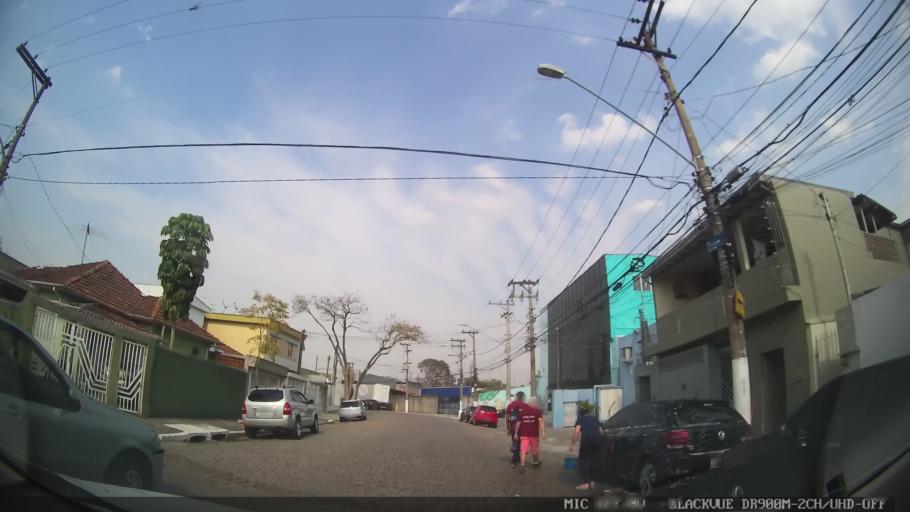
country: BR
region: Sao Paulo
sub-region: Sao Caetano Do Sul
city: Sao Caetano do Sul
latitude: -23.6017
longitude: -46.5931
